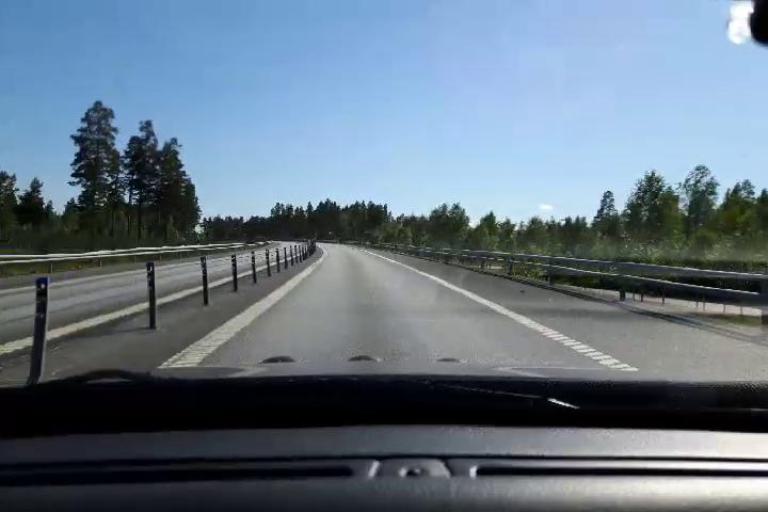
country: SE
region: Gaevleborg
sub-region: Gavle Kommun
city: Norrsundet
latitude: 61.0743
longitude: 16.9653
